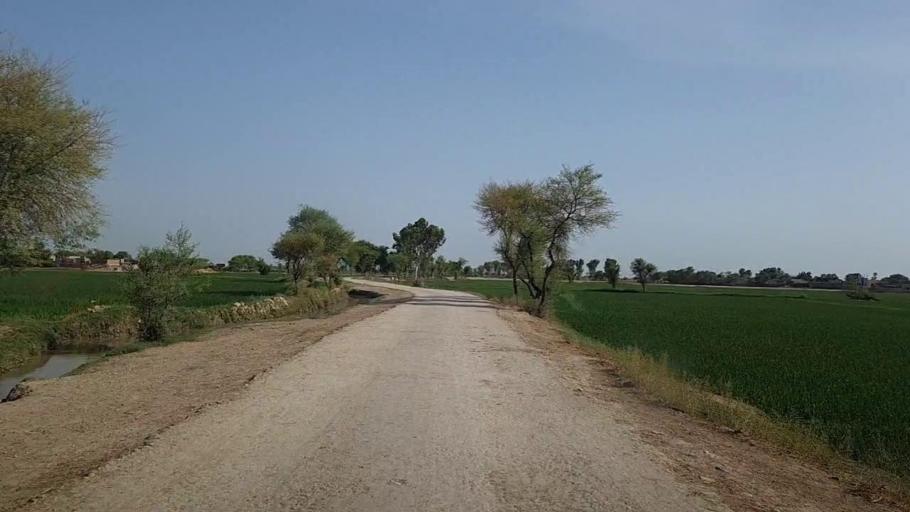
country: PK
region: Sindh
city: Sita Road
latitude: 27.0983
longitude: 67.8526
